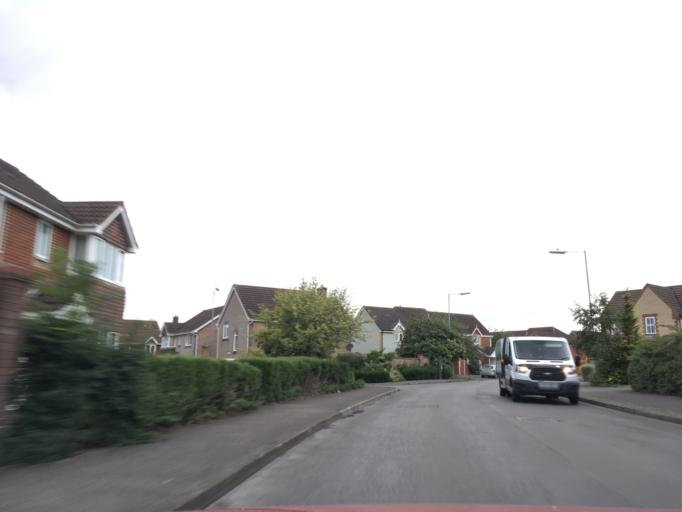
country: GB
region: England
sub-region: Wiltshire
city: Chippenham
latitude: 51.4473
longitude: -2.1105
